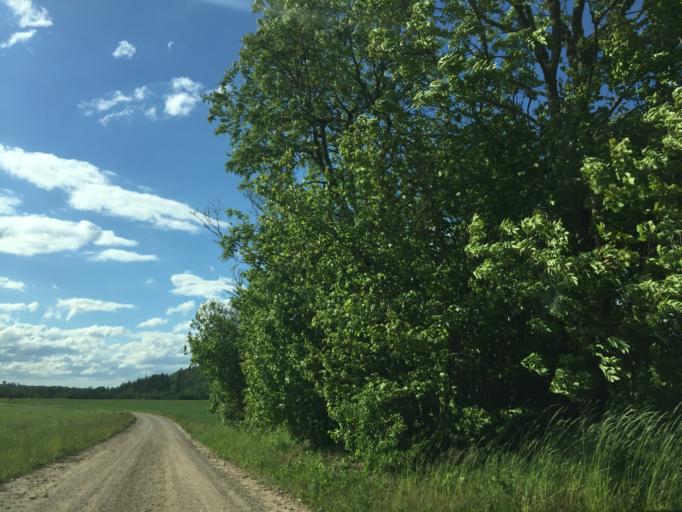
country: LV
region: Talsu Rajons
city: Sabile
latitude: 57.0124
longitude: 22.6325
